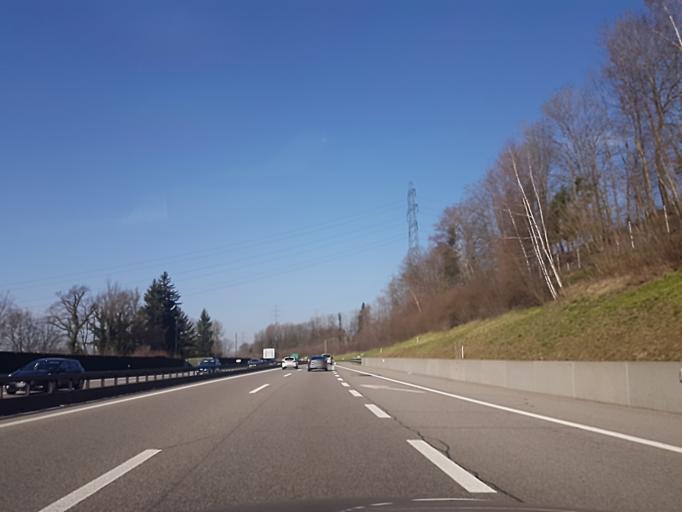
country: CH
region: Bern
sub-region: Oberaargau
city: Wangen an der Aare
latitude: 47.2377
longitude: 7.6428
